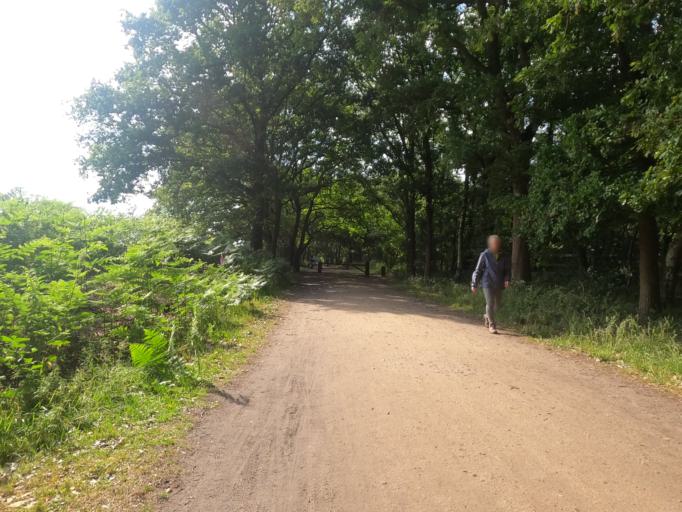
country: GB
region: England
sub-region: Cheshire West and Chester
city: Cuddington
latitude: 53.2124
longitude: -2.5929
